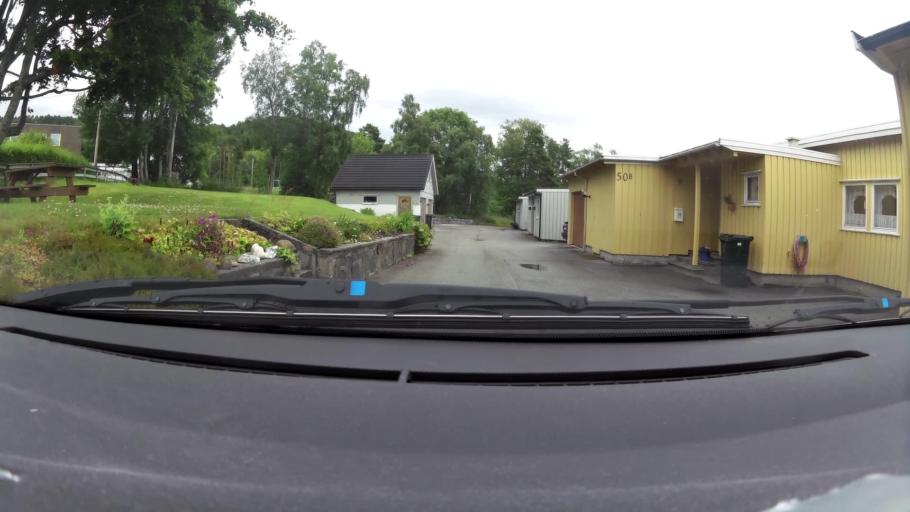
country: NO
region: More og Romsdal
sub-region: Molde
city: Molde
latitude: 62.7434
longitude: 7.1923
